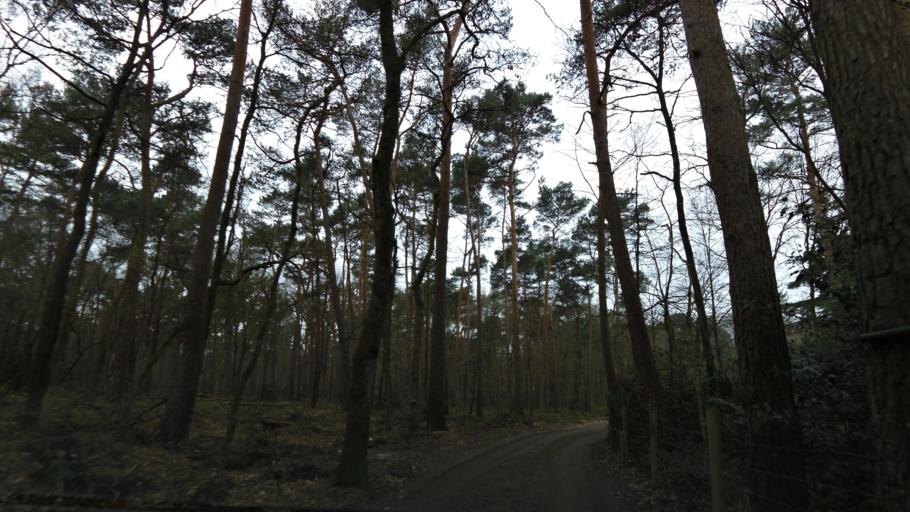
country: NL
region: Limburg
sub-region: Gemeente Onderbanken
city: Schinveld
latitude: 50.9612
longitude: 5.9910
